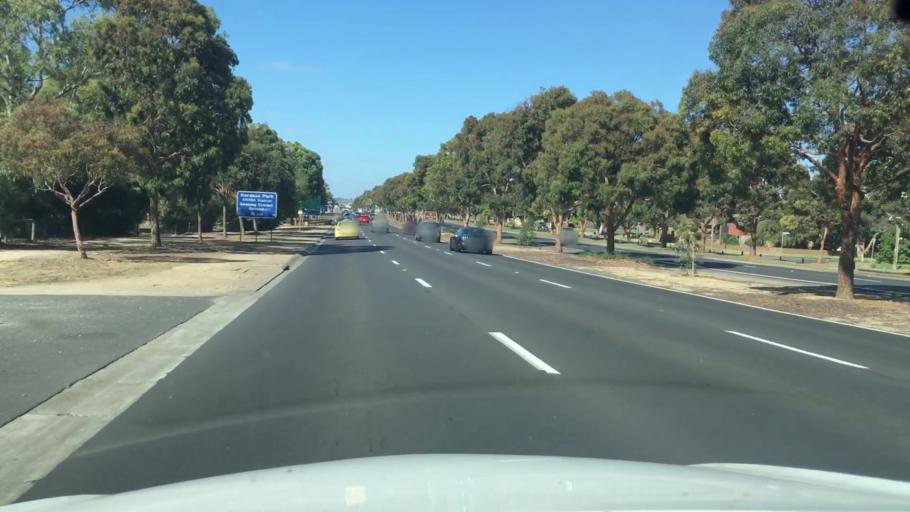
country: AU
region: Victoria
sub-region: Greater Geelong
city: Bell Park
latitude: -38.0727
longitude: 144.3724
